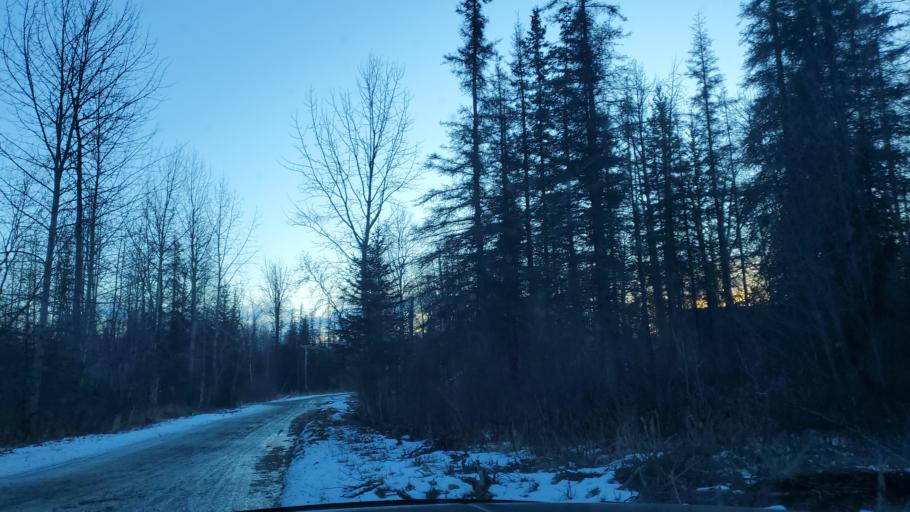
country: US
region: Alaska
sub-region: Matanuska-Susitna Borough
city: Lakes
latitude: 61.6668
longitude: -149.3409
